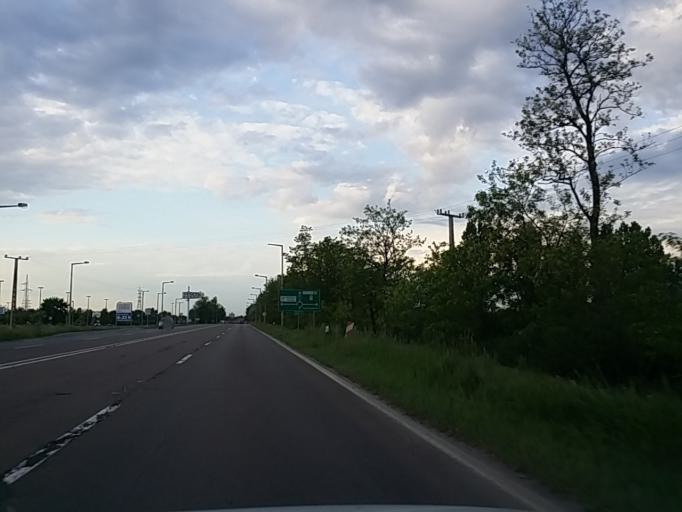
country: HU
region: Bacs-Kiskun
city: Kecskemet
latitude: 46.9349
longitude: 19.6627
